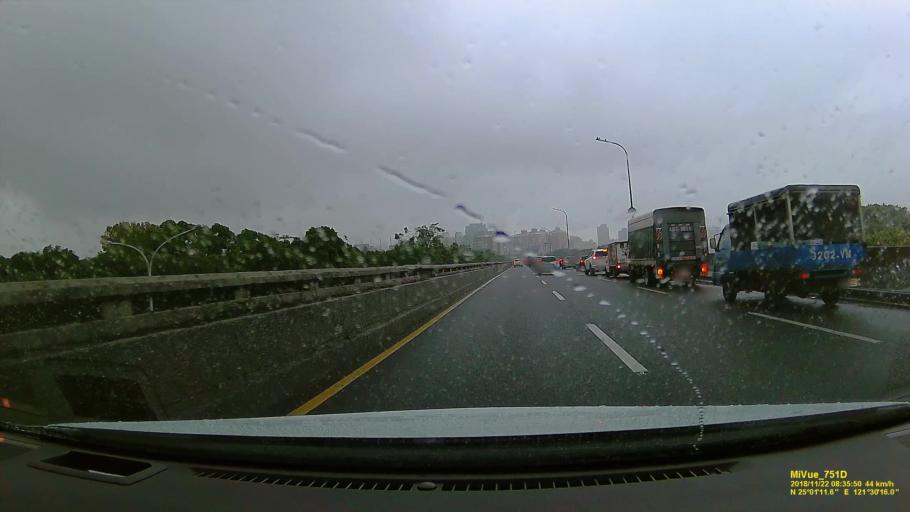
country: TW
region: Taipei
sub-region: Taipei
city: Banqiao
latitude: 25.0200
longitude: 121.5047
